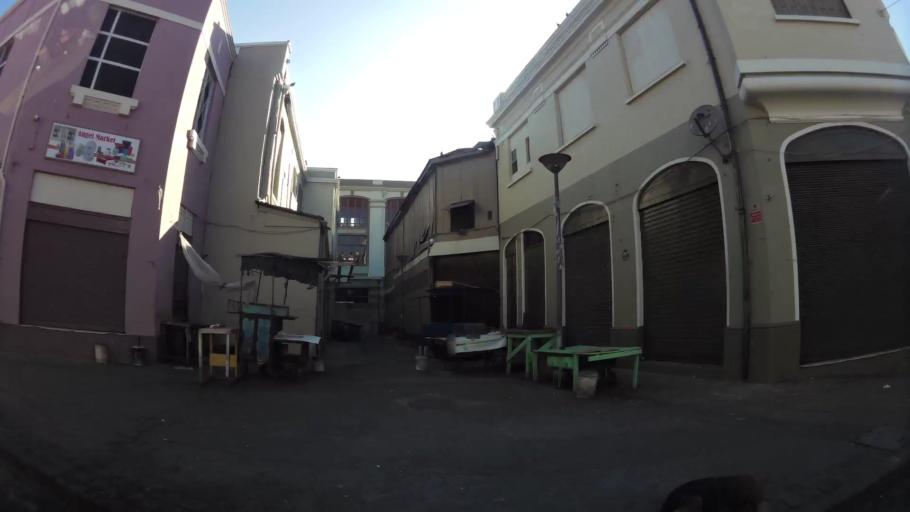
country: CL
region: Valparaiso
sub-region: Provincia de Valparaiso
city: Valparaiso
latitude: -33.0360
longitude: -71.6307
